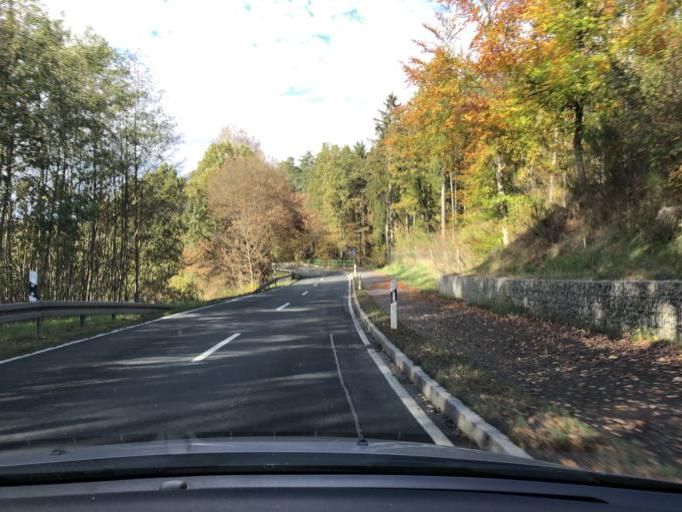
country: DE
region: Thuringia
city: Schleusingen
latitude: 50.4968
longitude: 10.7791
